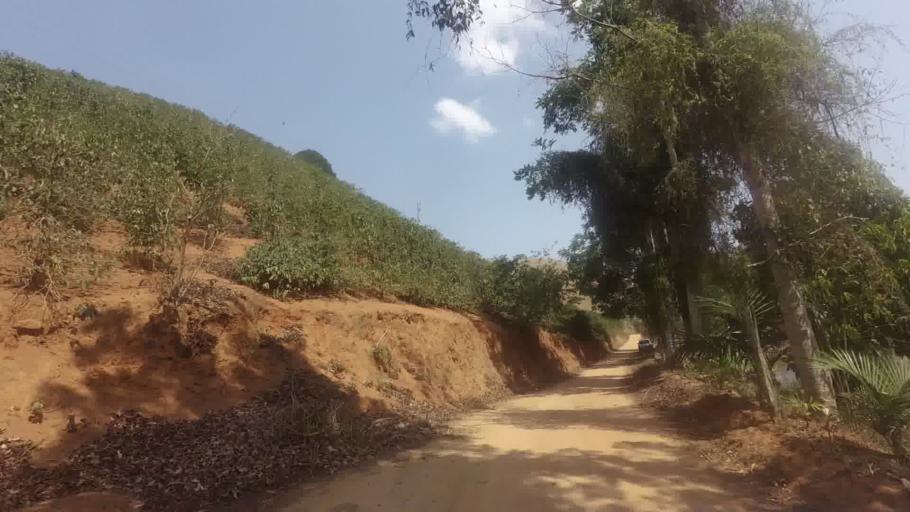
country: BR
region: Espirito Santo
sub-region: Mimoso Do Sul
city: Mimoso do Sul
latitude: -20.9899
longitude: -41.4998
